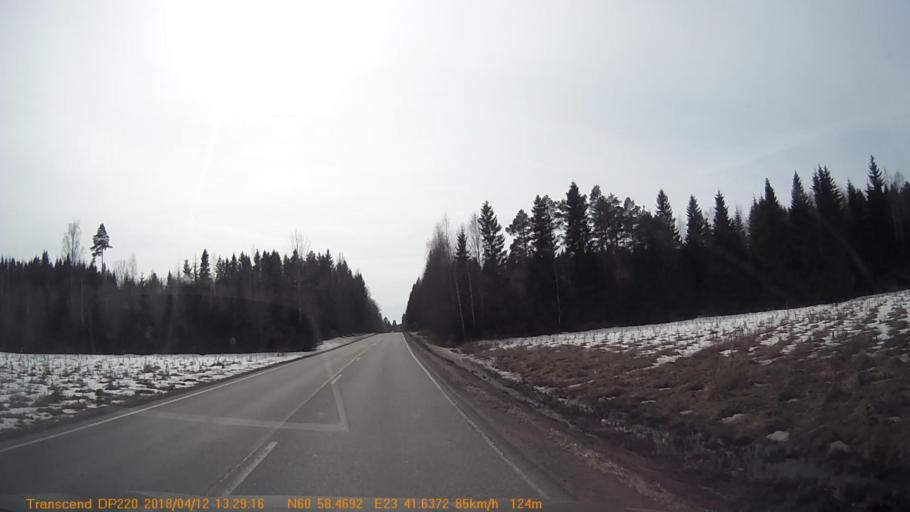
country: FI
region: Haeme
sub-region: Forssa
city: Forssa
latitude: 60.9743
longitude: 23.6937
